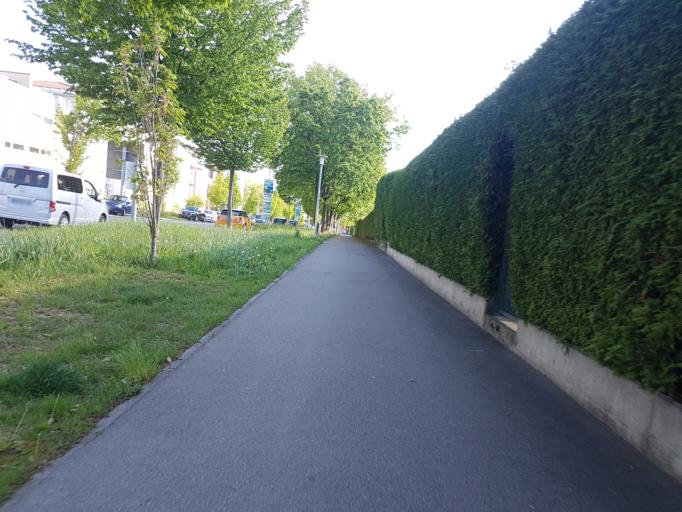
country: DE
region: Baden-Wuerttemberg
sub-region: Regierungsbezirk Stuttgart
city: Kornwestheim
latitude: 48.8542
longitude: 9.1847
